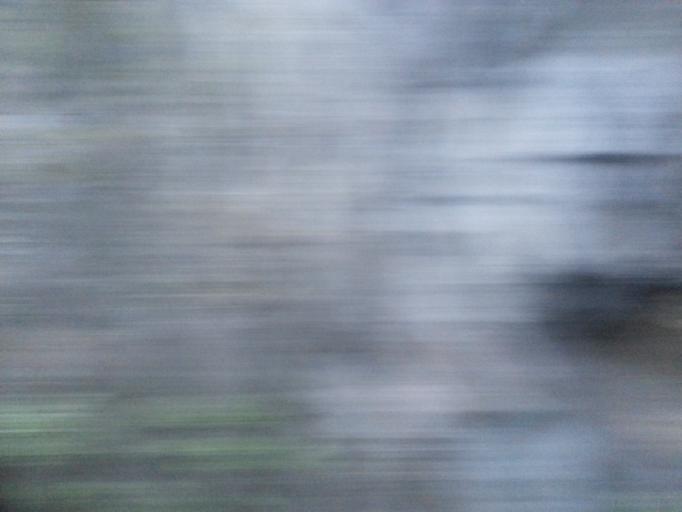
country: NO
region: Oppland
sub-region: Dovre
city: Dombas
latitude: 62.0722
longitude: 9.1277
